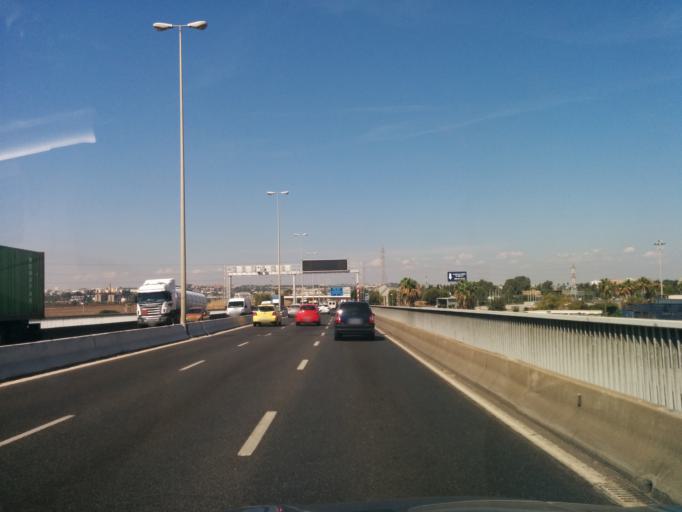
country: ES
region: Andalusia
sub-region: Provincia de Sevilla
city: Gelves
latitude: 37.3556
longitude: -6.0008
